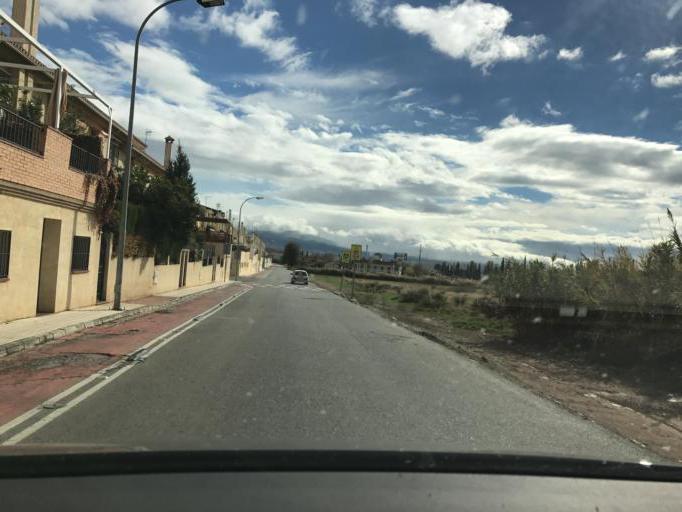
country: ES
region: Andalusia
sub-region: Provincia de Granada
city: Peligros
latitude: 37.2346
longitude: -3.6397
